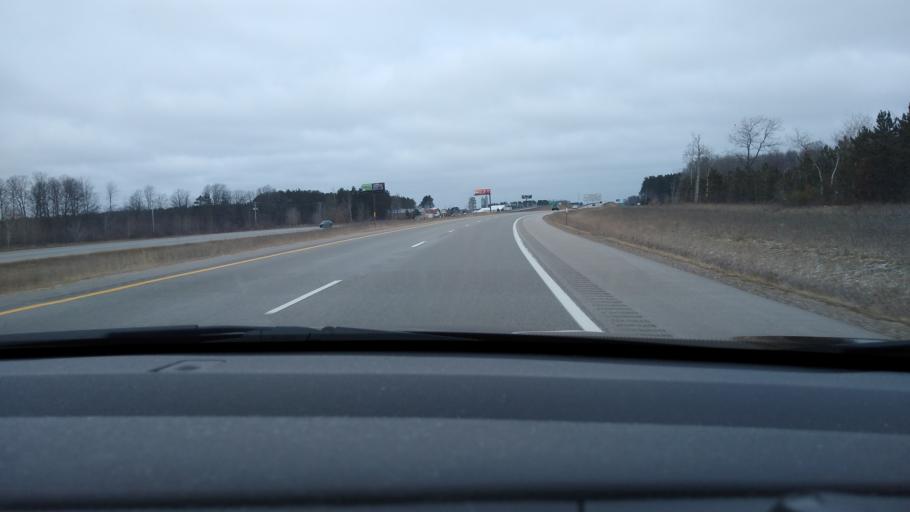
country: US
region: Michigan
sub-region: Otsego County
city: Gaylord
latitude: 44.9969
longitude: -84.6856
